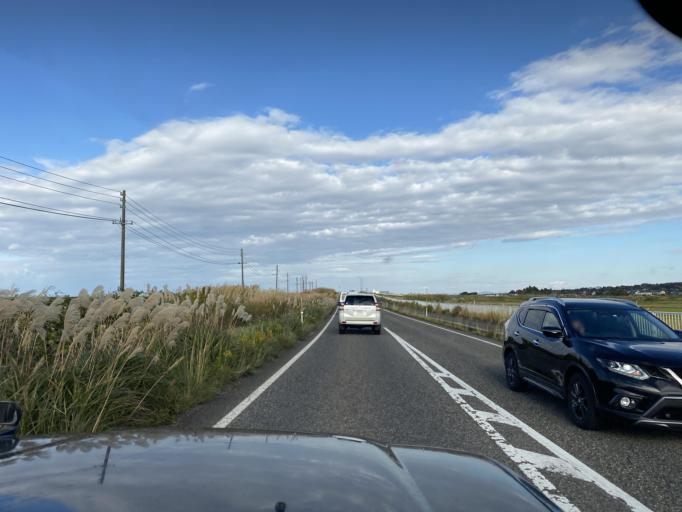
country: JP
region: Niigata
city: Niitsu-honcho
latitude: 37.7746
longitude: 139.1054
